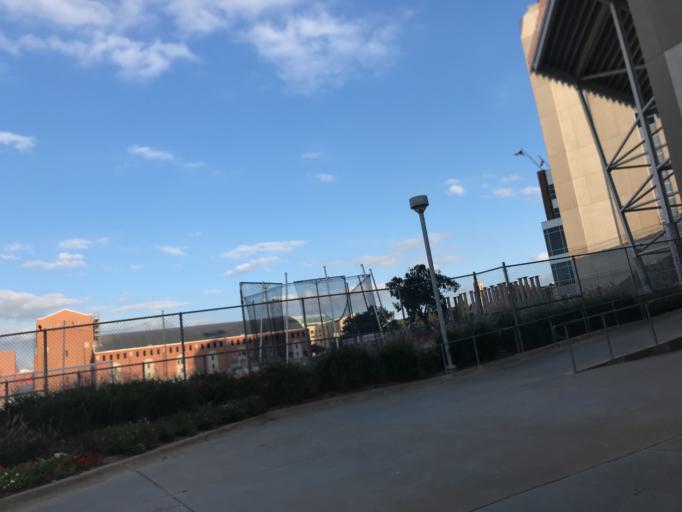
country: US
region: Nebraska
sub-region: Lancaster County
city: Lincoln
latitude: 40.8220
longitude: -96.7054
